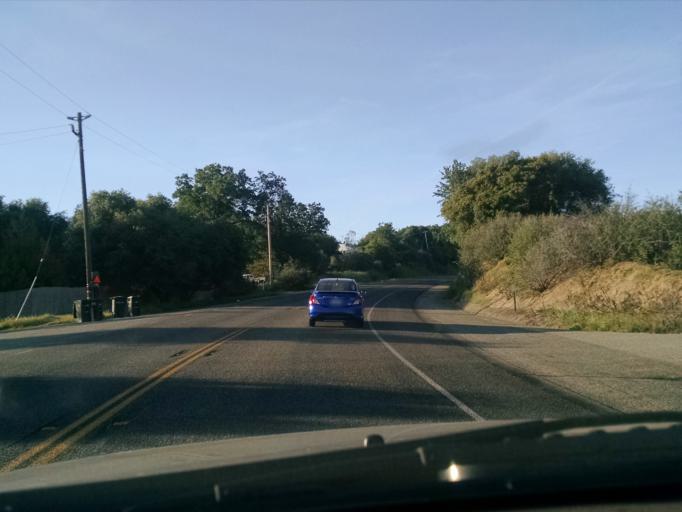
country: US
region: California
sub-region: Madera County
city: Ahwahnee
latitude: 37.3949
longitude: -119.7377
